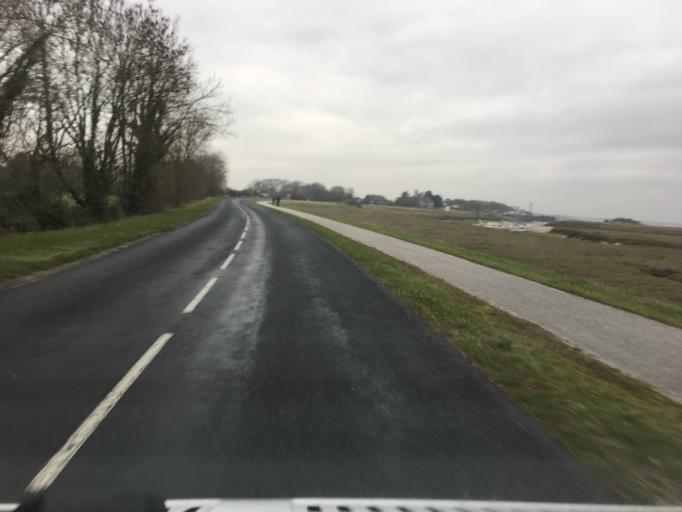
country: FR
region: Picardie
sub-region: Departement de la Somme
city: Pende
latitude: 50.2107
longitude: 1.5579
